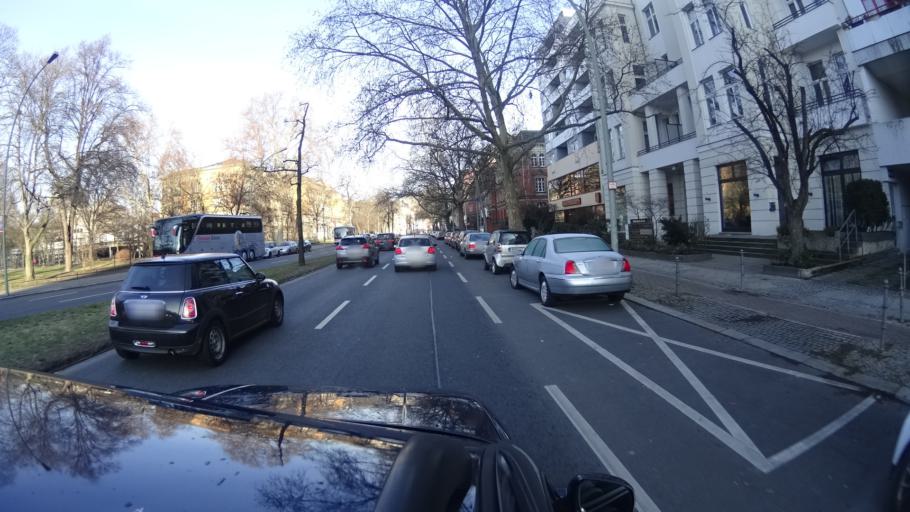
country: DE
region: Berlin
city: Wilmersdorf Bezirk
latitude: 52.4970
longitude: 13.3308
